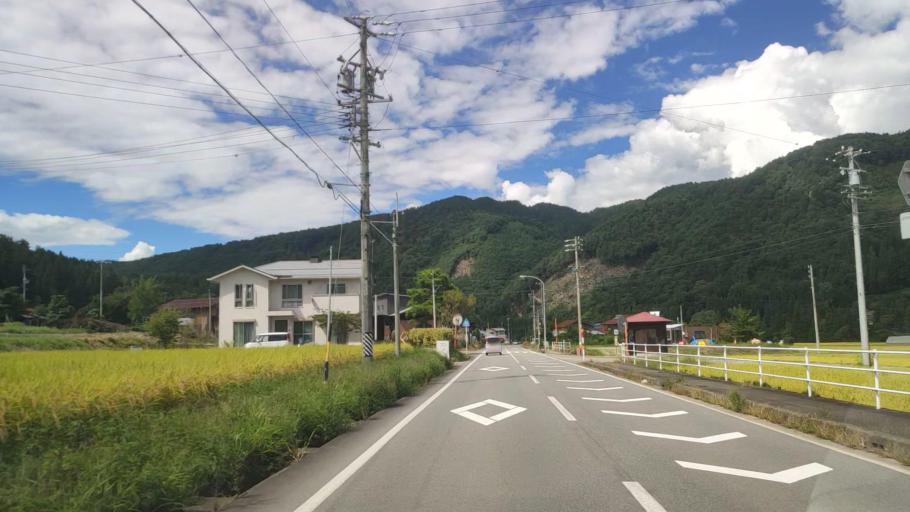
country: JP
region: Gifu
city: Takayama
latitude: 36.1766
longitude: 137.2844
